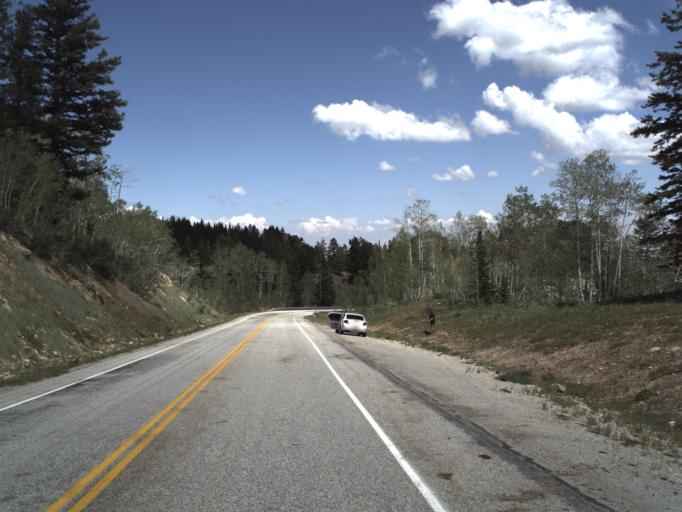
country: US
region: Utah
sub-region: Rich County
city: Randolph
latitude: 41.4733
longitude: -111.4730
